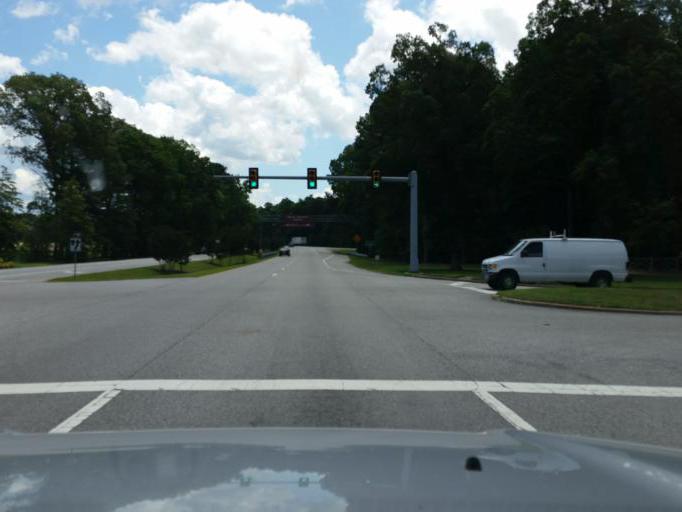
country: US
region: Virginia
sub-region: City of Williamsburg
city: Williamsburg
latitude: 37.2437
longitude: -76.6559
